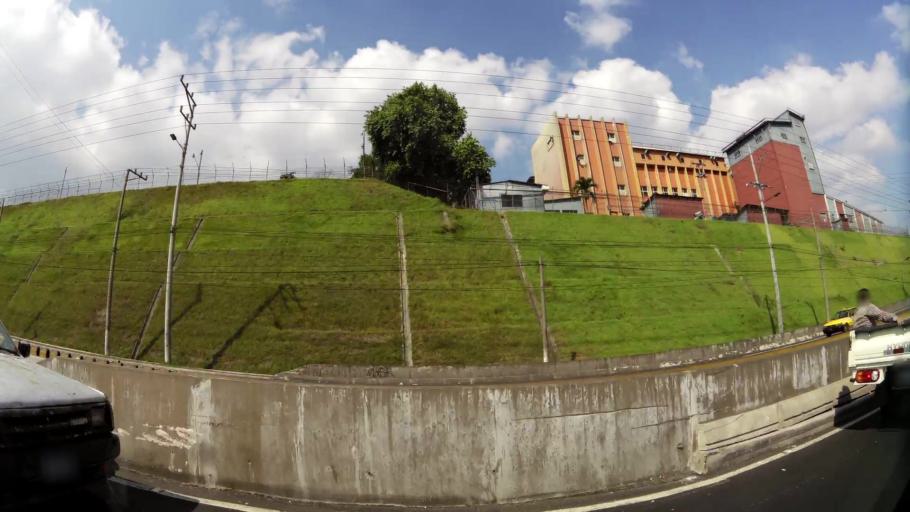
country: SV
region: San Salvador
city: San Salvador
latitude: 13.6999
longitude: -89.1705
